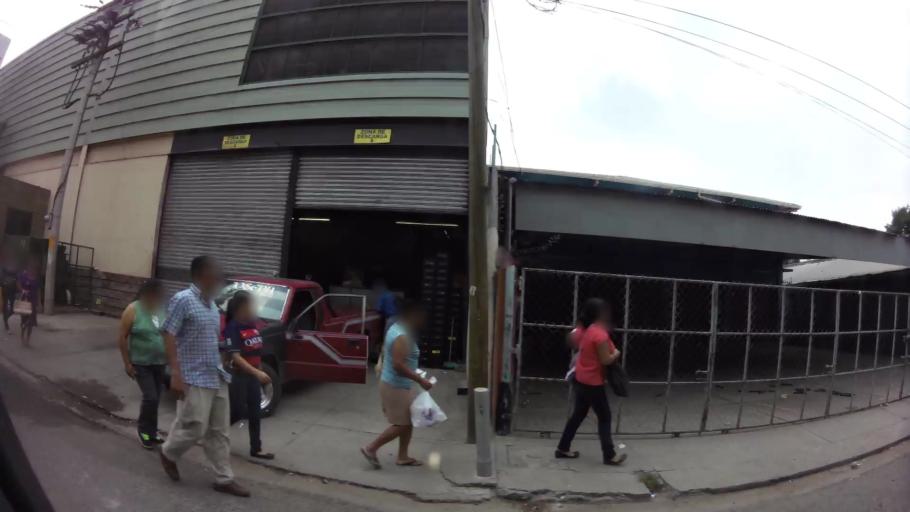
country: HN
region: Comayagua
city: Siguatepeque
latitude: 14.5941
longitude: -87.8317
